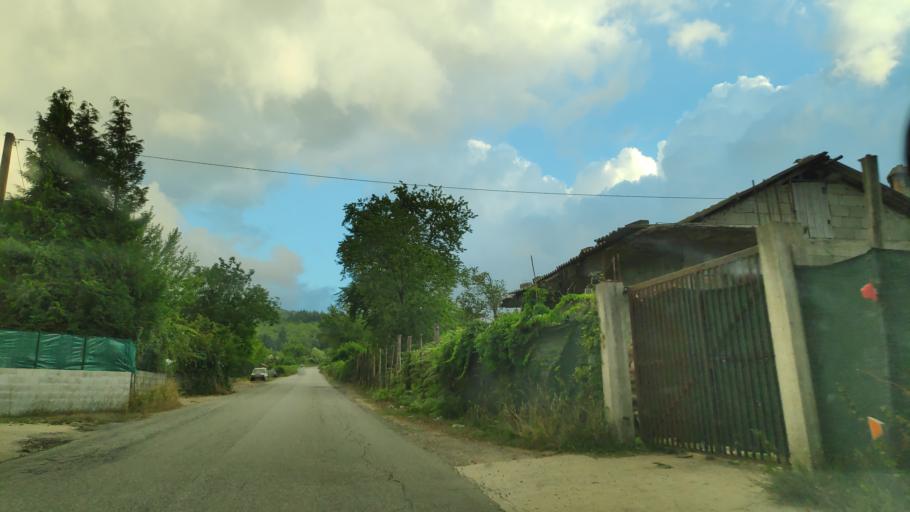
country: IT
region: Calabria
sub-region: Provincia di Vibo-Valentia
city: Serra San Bruno
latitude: 38.5587
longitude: 16.3264
